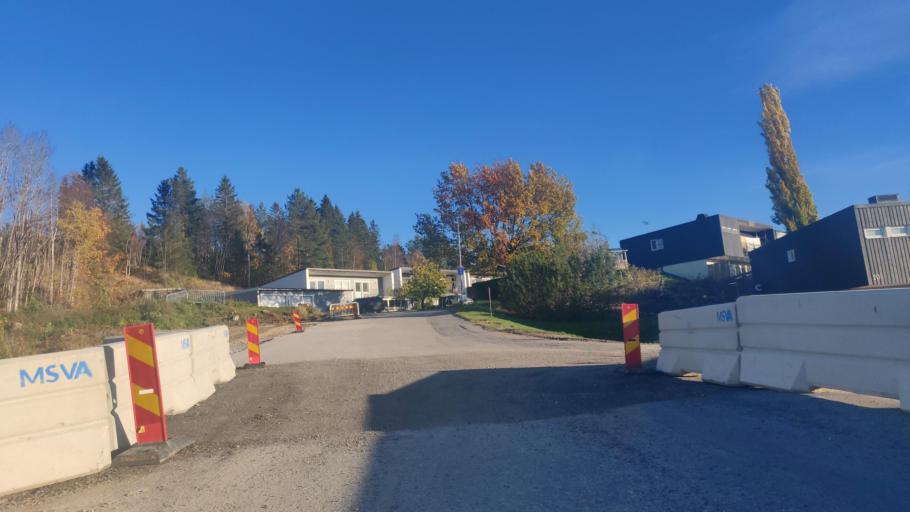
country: SE
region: Vaesternorrland
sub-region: Sundsvalls Kommun
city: Njurundabommen
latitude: 62.2756
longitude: 17.3961
